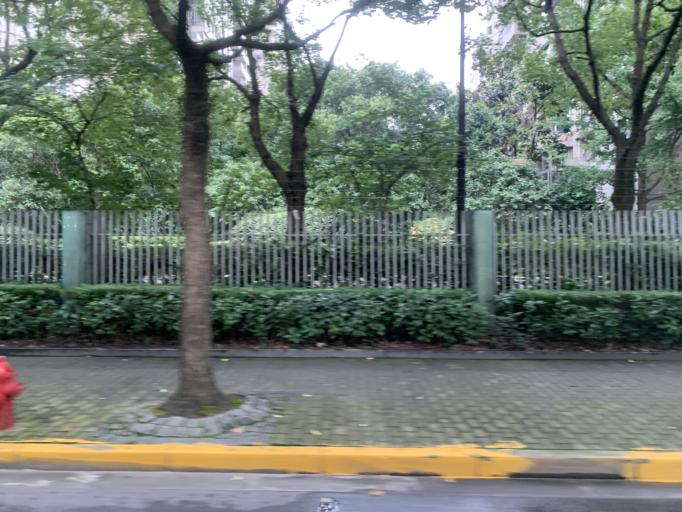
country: CN
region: Shanghai Shi
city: Huamu
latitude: 31.2287
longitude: 121.5618
